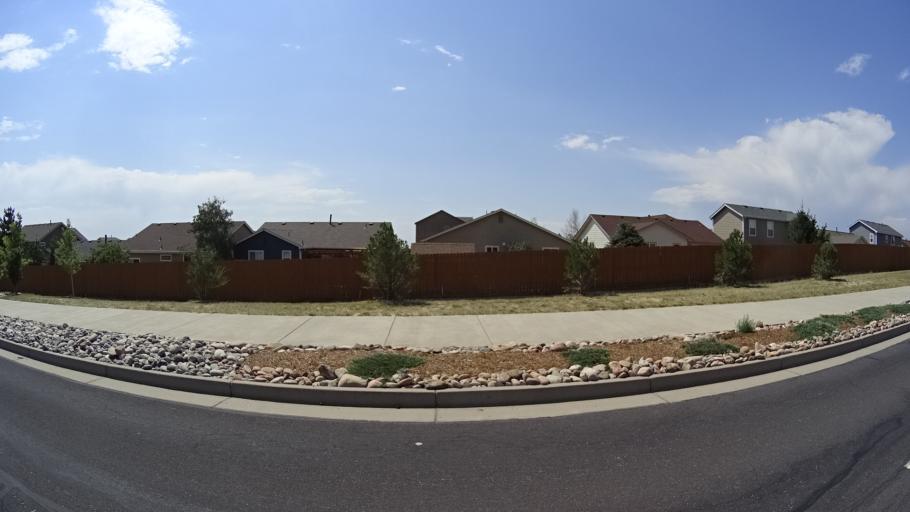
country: US
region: Colorado
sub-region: El Paso County
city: Cimarron Hills
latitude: 38.9259
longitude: -104.7078
